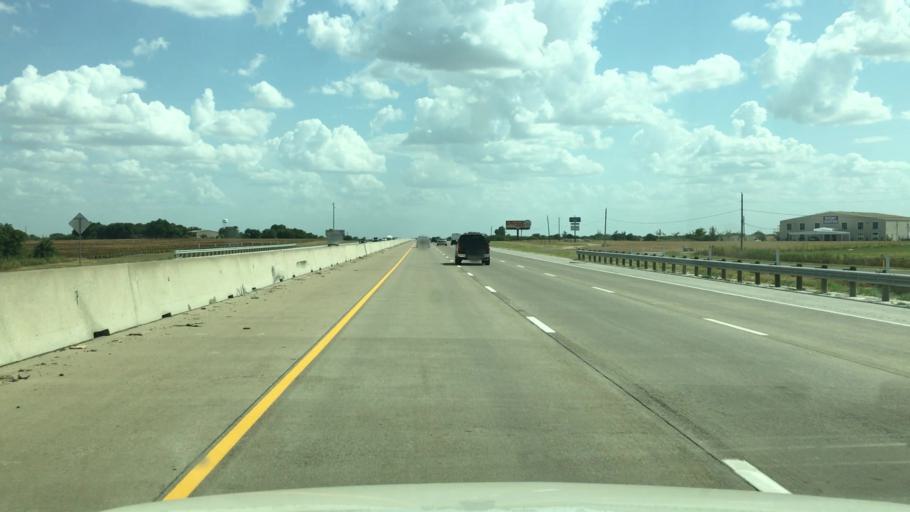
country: US
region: Texas
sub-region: Ellis County
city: Waxahachie
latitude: 32.3208
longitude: -96.8604
